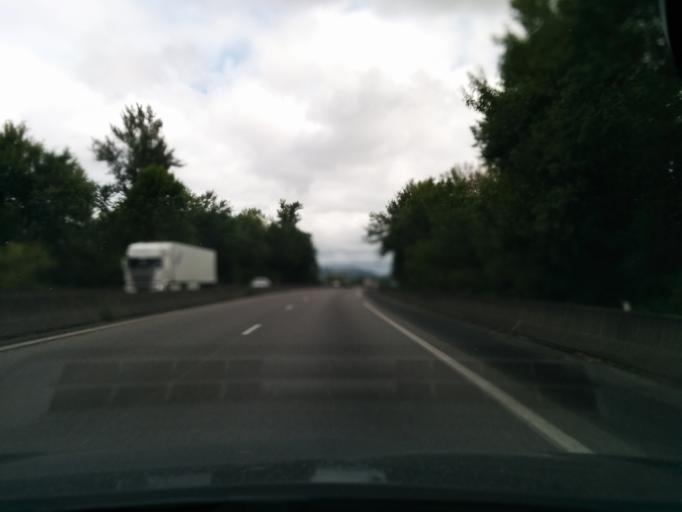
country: FR
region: Limousin
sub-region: Departement de la Correze
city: Ussac
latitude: 45.1907
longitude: 1.4942
